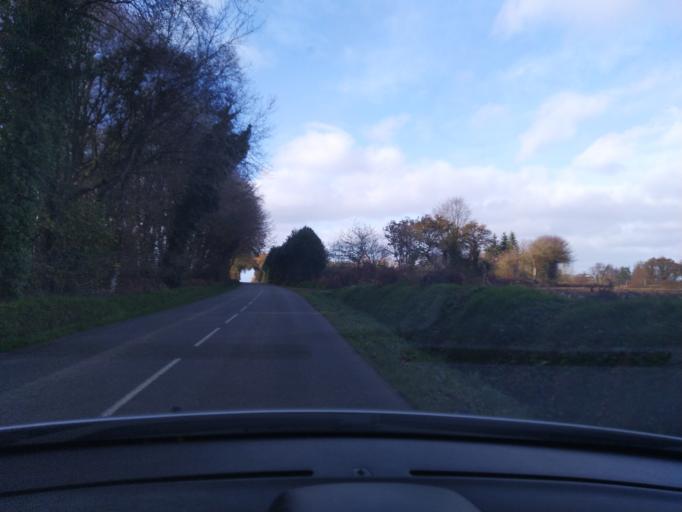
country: FR
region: Brittany
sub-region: Departement du Finistere
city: Plouigneau
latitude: 48.5529
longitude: -3.6871
